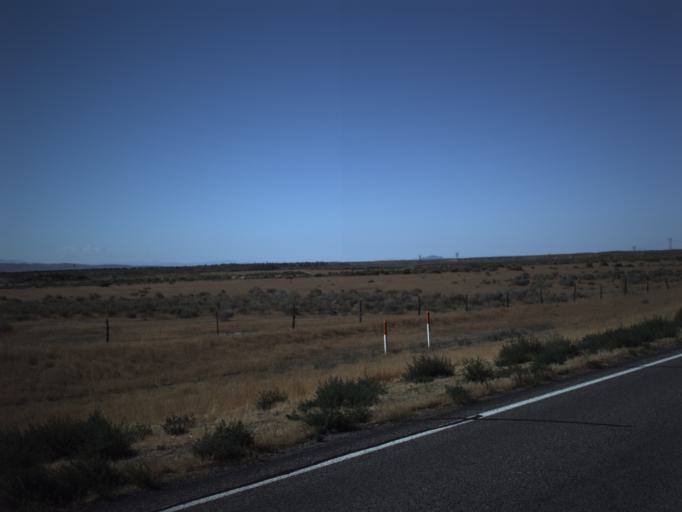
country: US
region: Utah
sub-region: Millard County
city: Delta
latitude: 39.5089
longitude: -112.3818
